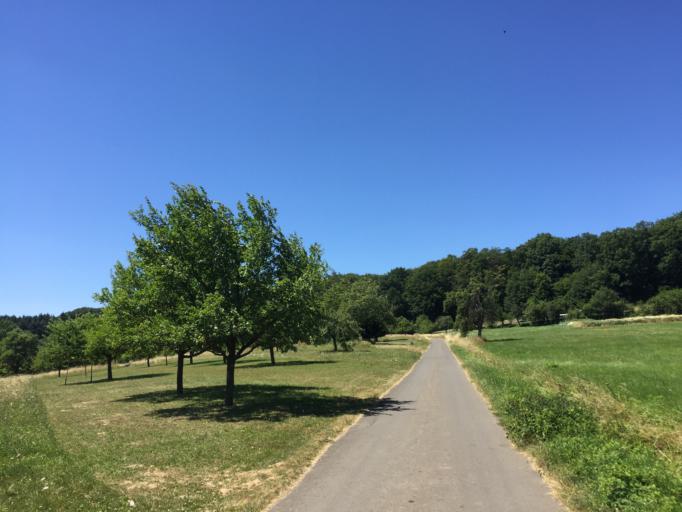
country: DE
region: Hesse
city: Beuern
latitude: 50.6318
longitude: 8.8172
